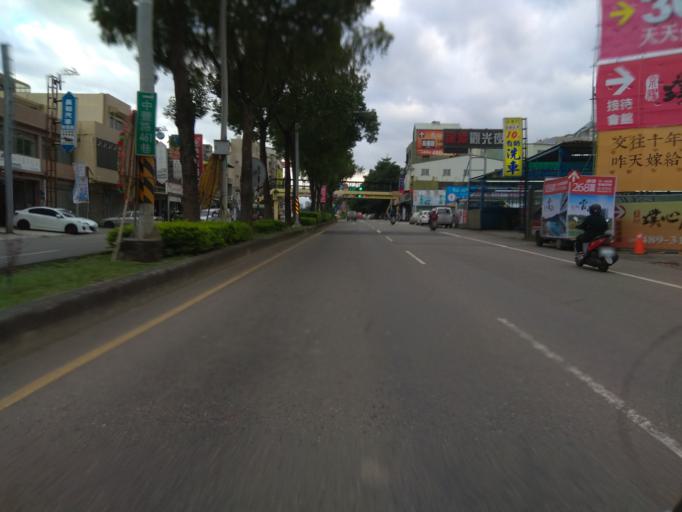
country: TW
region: Taiwan
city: Daxi
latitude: 24.8822
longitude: 121.2118
